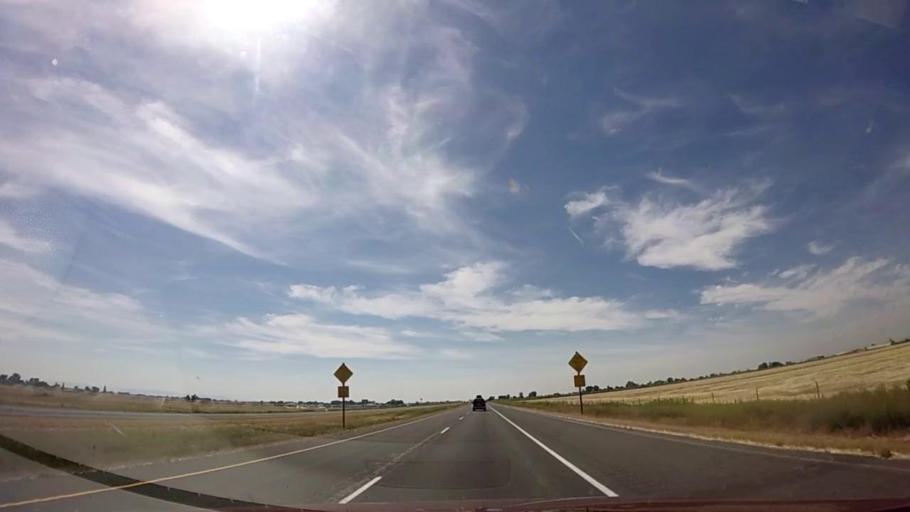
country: US
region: Idaho
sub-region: Minidoka County
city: Heyburn
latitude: 42.5690
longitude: -113.7109
